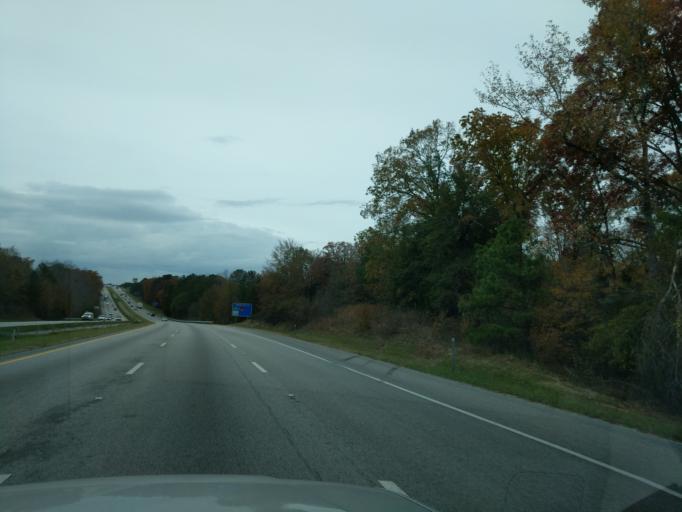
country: US
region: South Carolina
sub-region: Laurens County
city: Clinton
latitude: 34.4987
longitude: -81.8463
